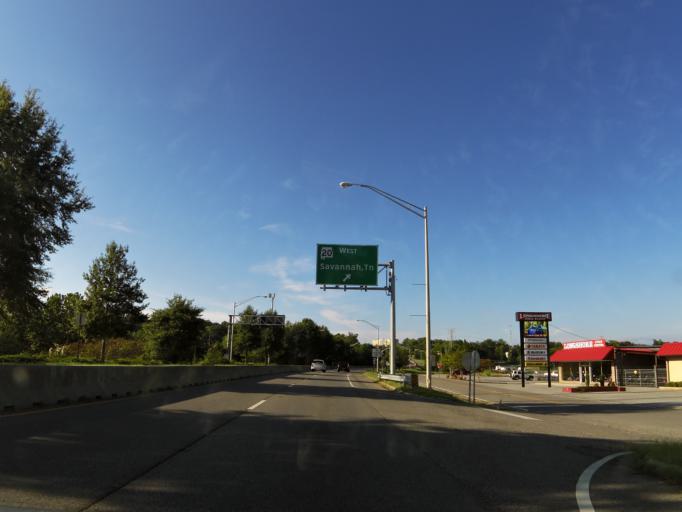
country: US
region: Alabama
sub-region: Lauderdale County
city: Florence
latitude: 34.7887
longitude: -87.6734
